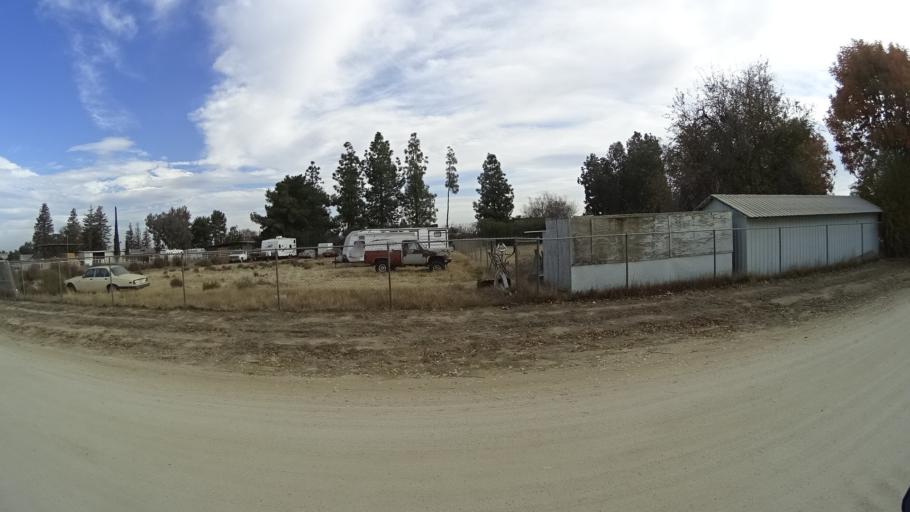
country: US
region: California
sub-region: Kern County
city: Rosedale
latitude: 35.4280
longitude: -119.1389
